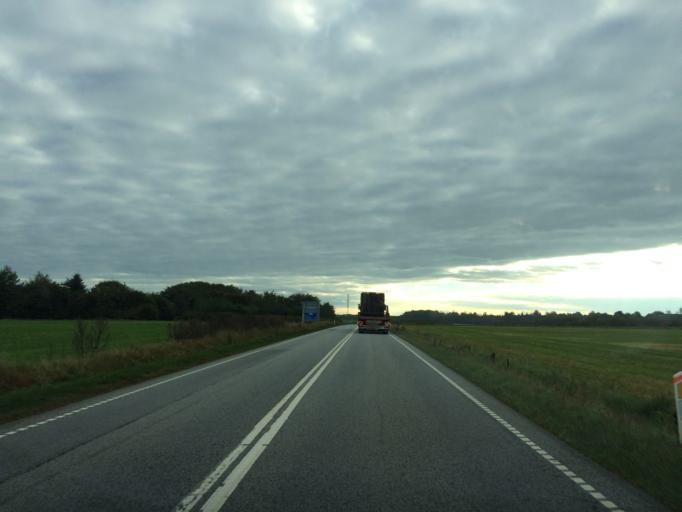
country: DK
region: Central Jutland
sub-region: Ringkobing-Skjern Kommune
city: Tarm
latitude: 55.9675
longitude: 8.5791
